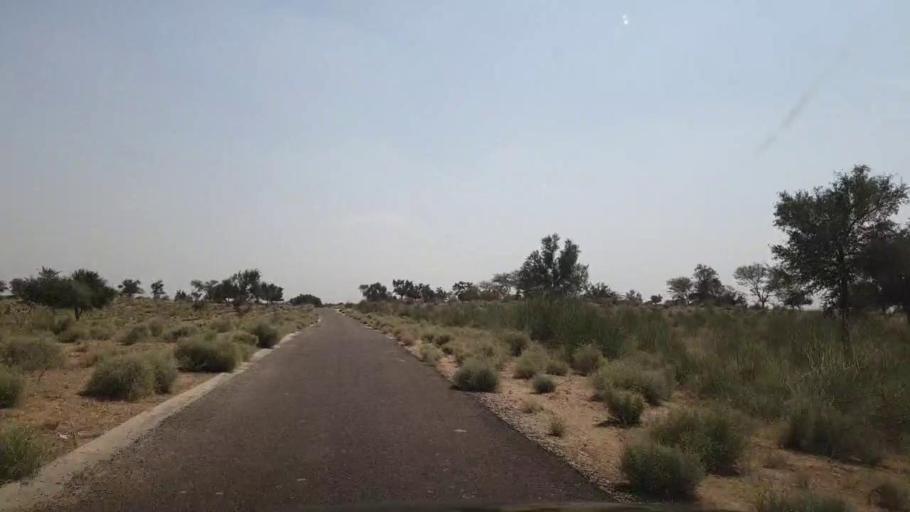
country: PK
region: Sindh
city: Islamkot
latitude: 25.0966
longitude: 70.7287
